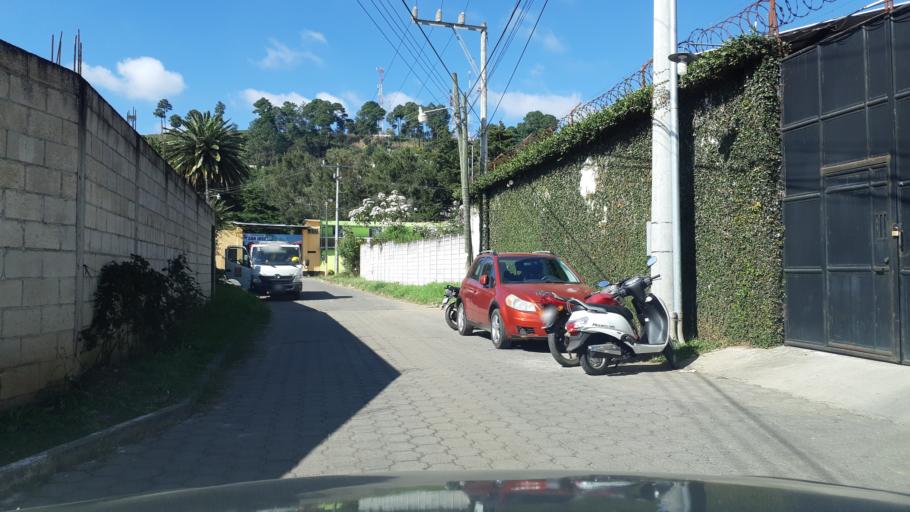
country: GT
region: Chimaltenango
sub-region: Municipio de Chimaltenango
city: Chimaltenango
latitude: 14.6519
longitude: -90.8179
